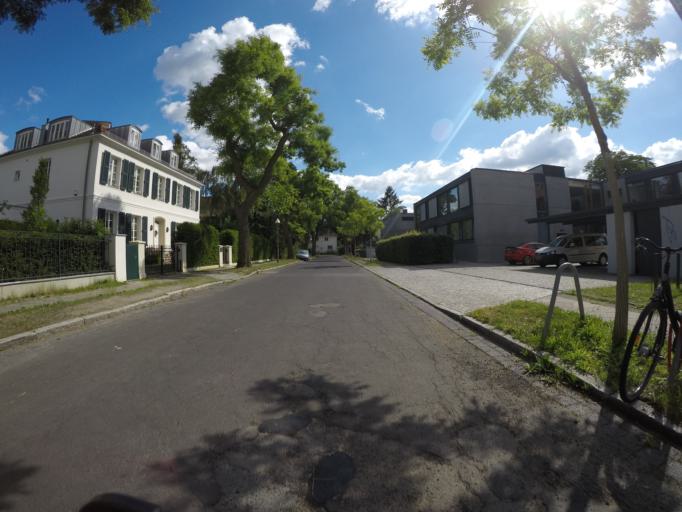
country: DE
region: Berlin
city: Dahlem
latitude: 52.4459
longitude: 13.2781
